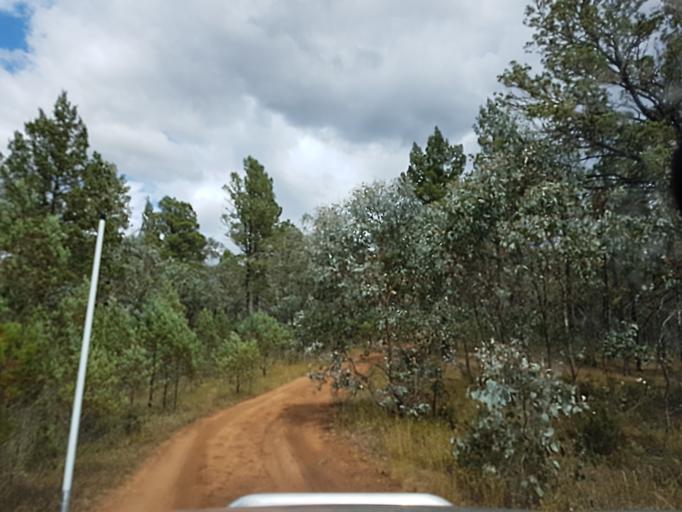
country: AU
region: New South Wales
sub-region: Snowy River
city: Jindabyne
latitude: -36.9300
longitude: 148.3938
